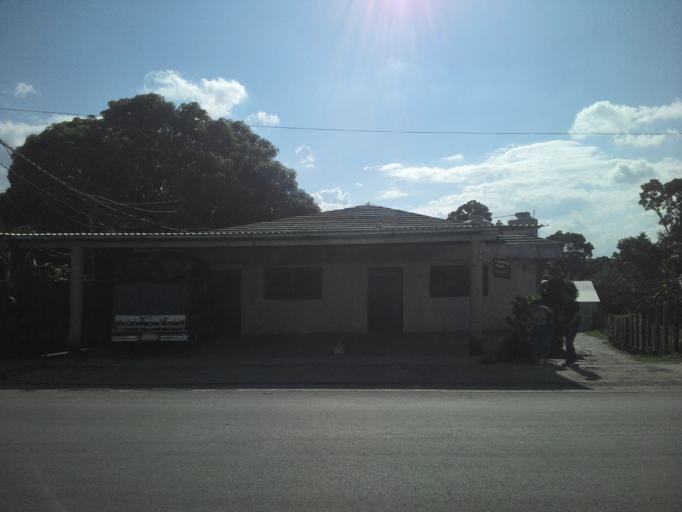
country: MX
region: Chiapas
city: Palenque
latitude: 17.5132
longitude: -91.9920
